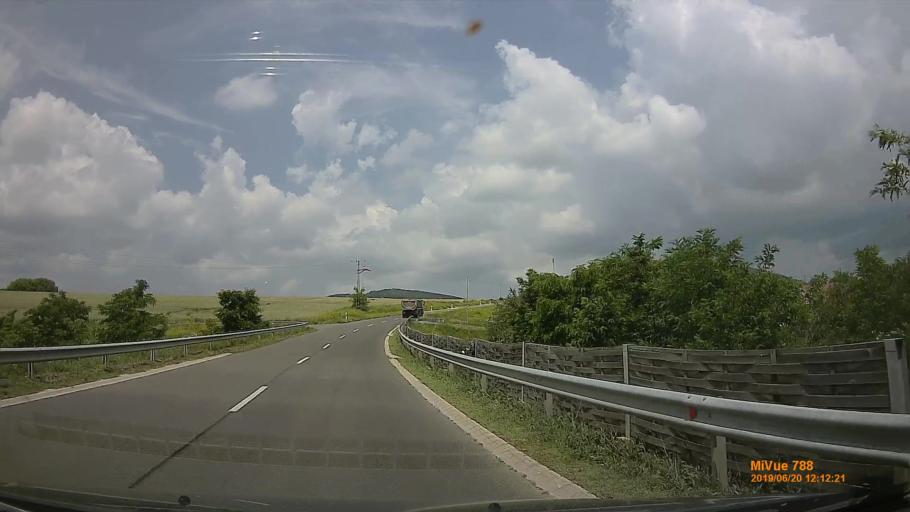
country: HU
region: Baranya
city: Hosszuheteny
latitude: 46.1461
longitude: 18.3473
